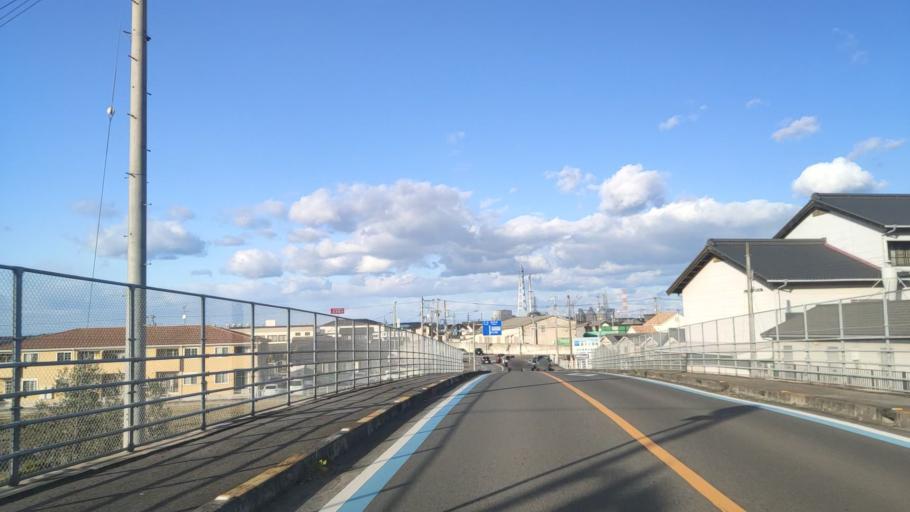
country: JP
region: Ehime
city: Saijo
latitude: 33.9139
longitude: 133.1620
